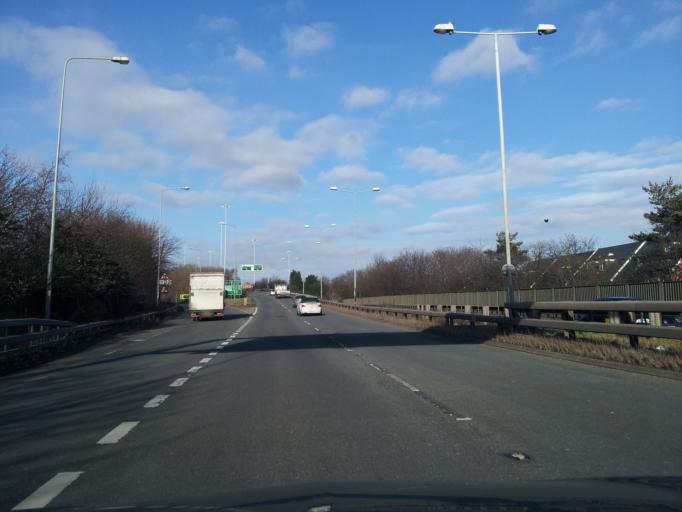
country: GB
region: England
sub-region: Nottinghamshire
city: Ruddington
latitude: 52.9198
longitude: -1.1626
